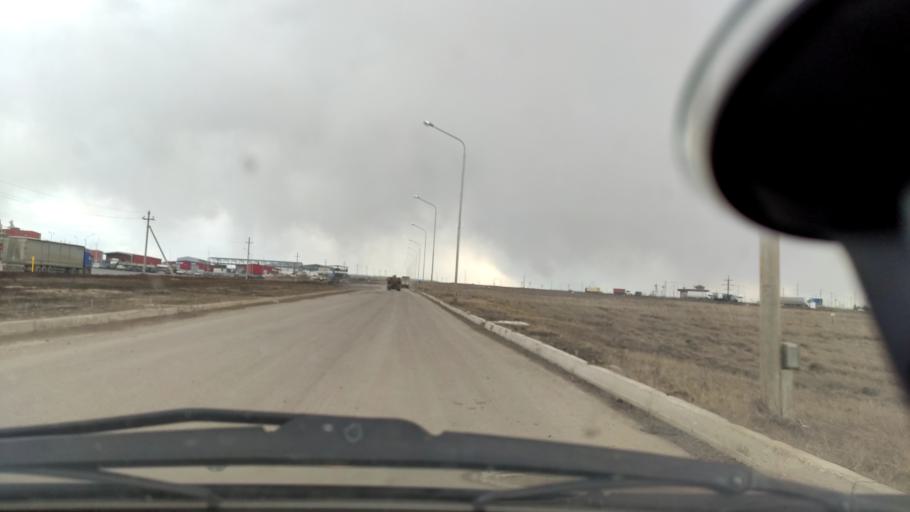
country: RU
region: Bashkortostan
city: Iglino
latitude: 54.7696
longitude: 56.2635
